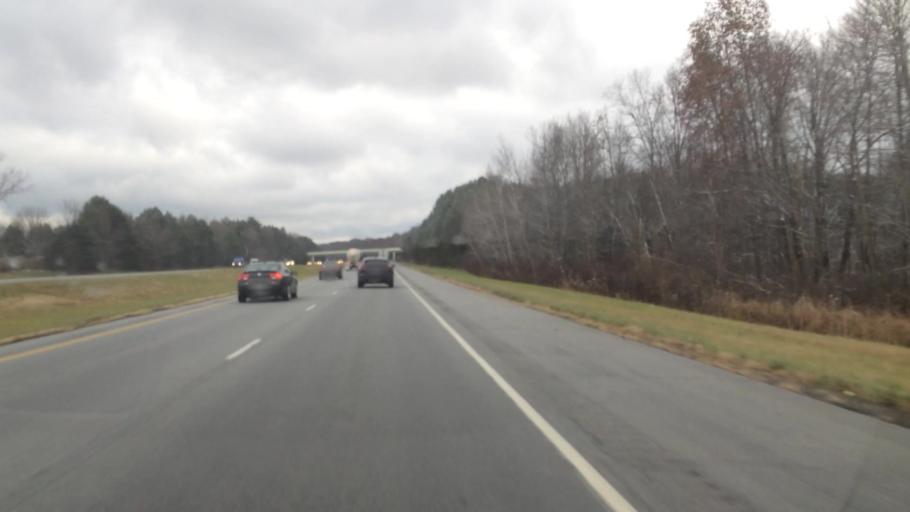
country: US
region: Ohio
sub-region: Summit County
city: Twinsburg
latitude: 41.2888
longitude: -81.4217
